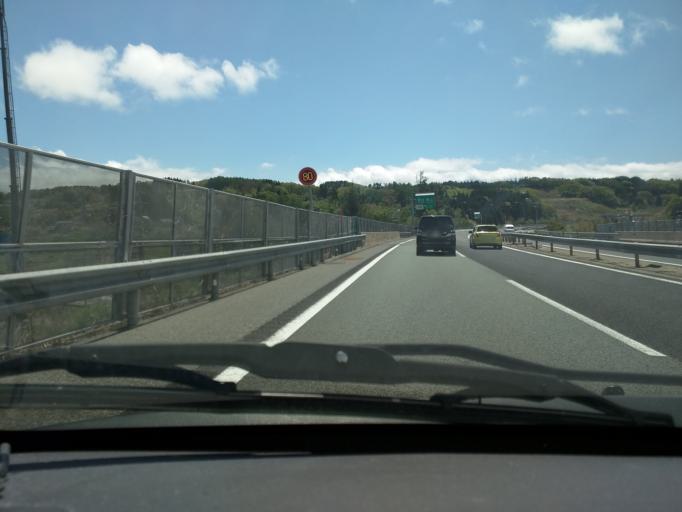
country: JP
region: Nagano
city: Iiyama
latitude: 36.8004
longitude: 138.3182
